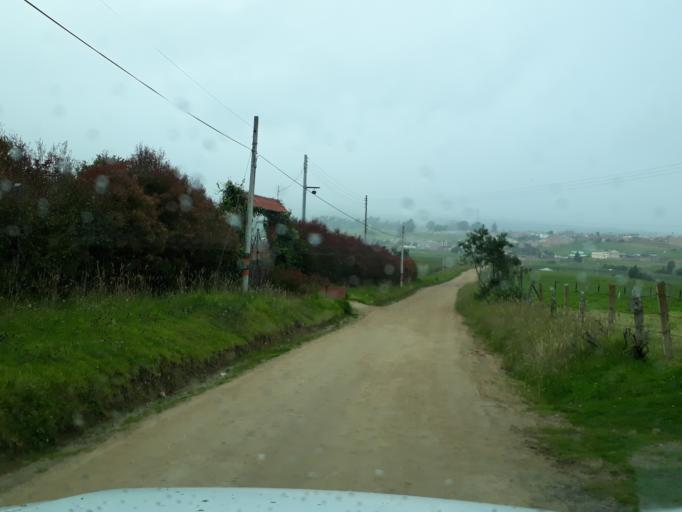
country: CO
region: Cundinamarca
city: Guasca
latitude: 4.8767
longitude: -73.8746
